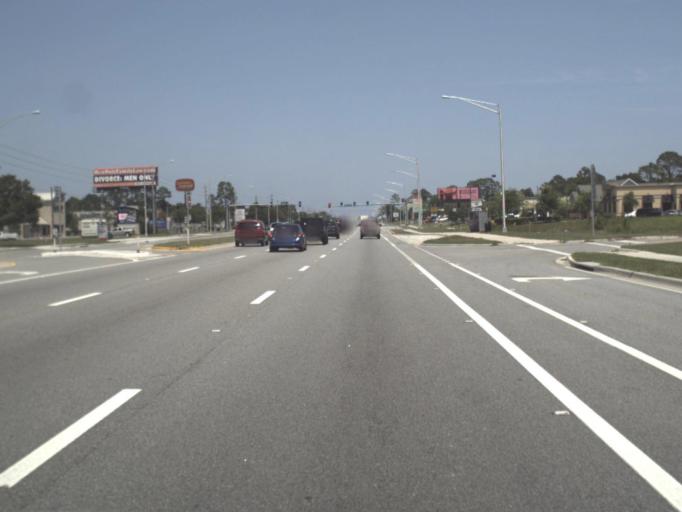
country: US
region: Florida
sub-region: Duval County
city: Jacksonville Beach
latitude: 30.2876
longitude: -81.4511
